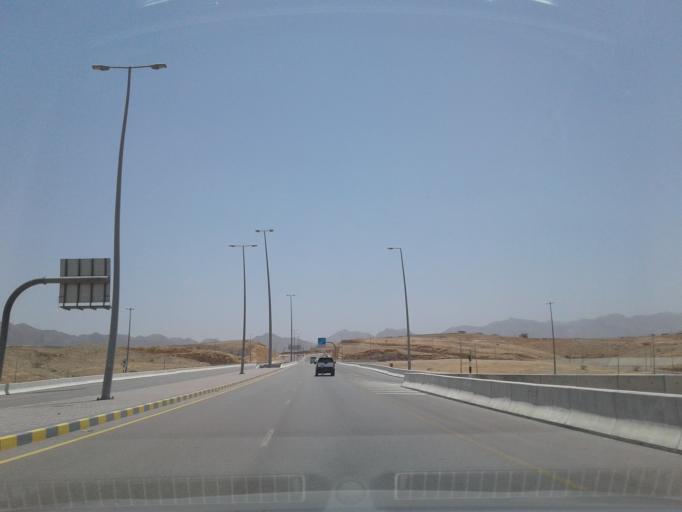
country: OM
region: Muhafazat Masqat
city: Bawshar
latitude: 23.5628
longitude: 58.3386
